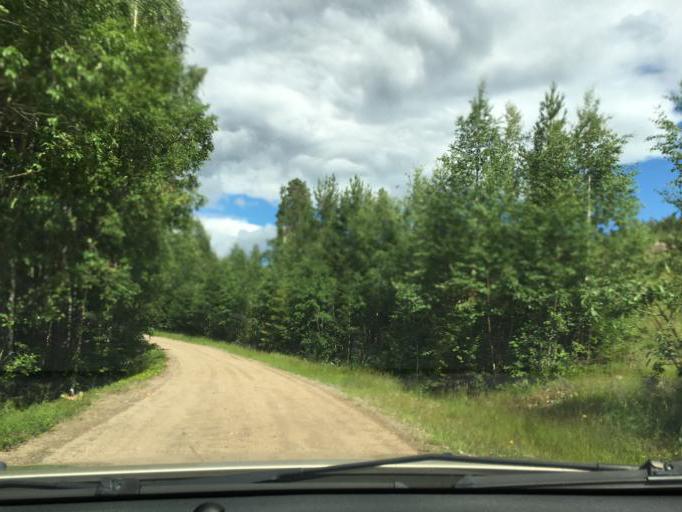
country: SE
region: Norrbotten
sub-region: Overkalix Kommun
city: OEverkalix
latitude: 66.1552
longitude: 22.8588
